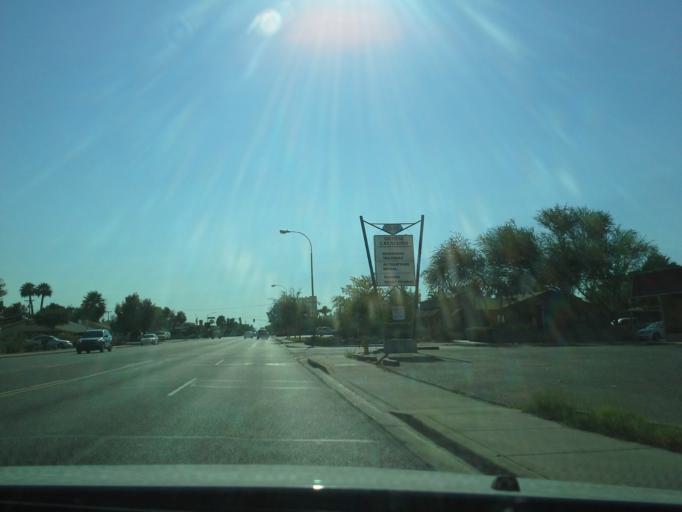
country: US
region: Arizona
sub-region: Maricopa County
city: Paradise Valley
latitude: 33.4952
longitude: -111.9971
